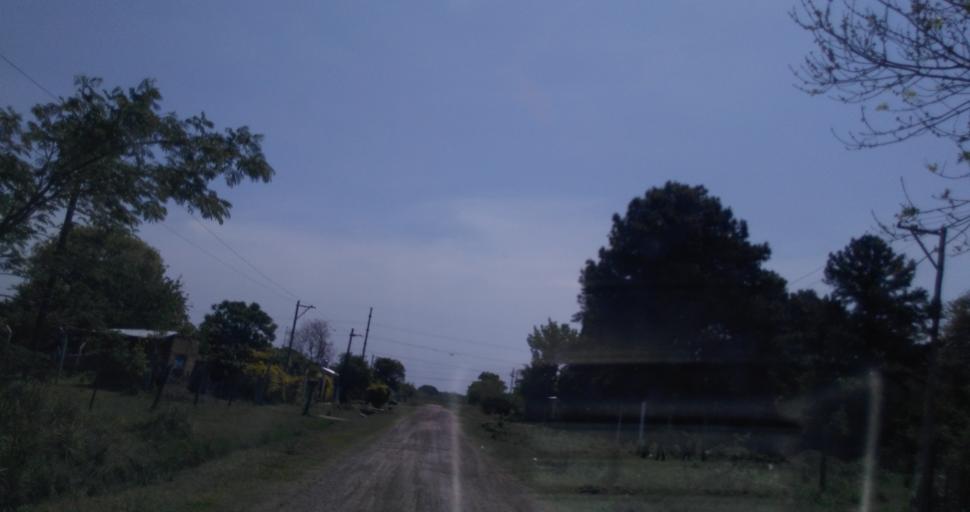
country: AR
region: Chaco
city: Fontana
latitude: -27.4037
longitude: -59.0039
